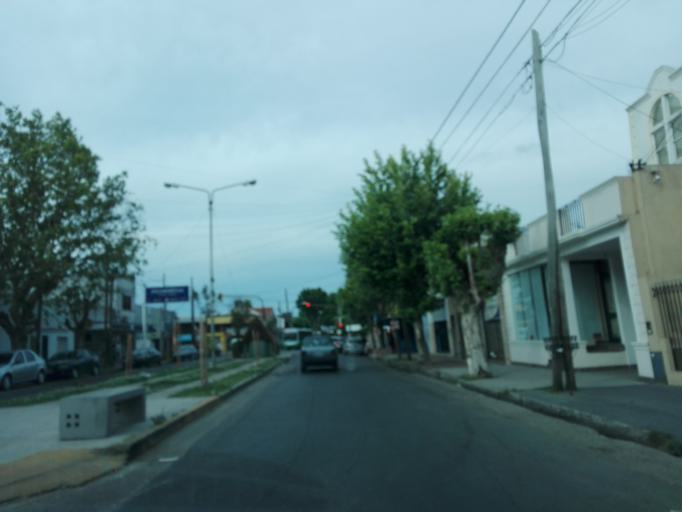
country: AR
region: Buenos Aires
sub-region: Partido de Lanus
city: Lanus
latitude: -34.7117
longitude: -58.3774
